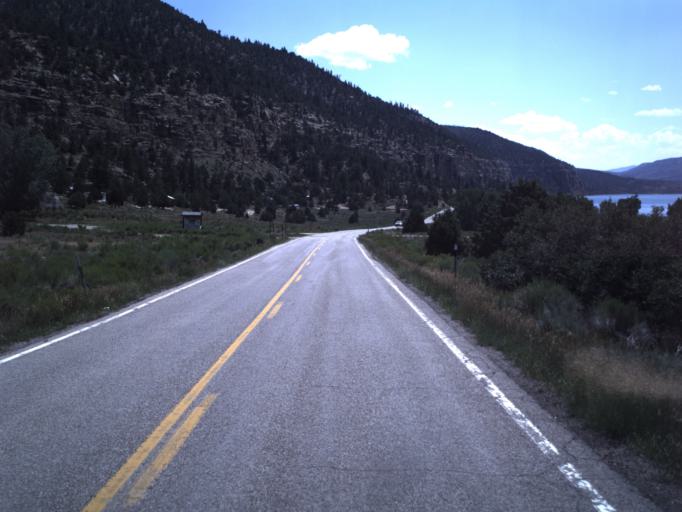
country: US
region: Utah
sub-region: Emery County
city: Orangeville
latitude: 39.3097
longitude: -111.2739
